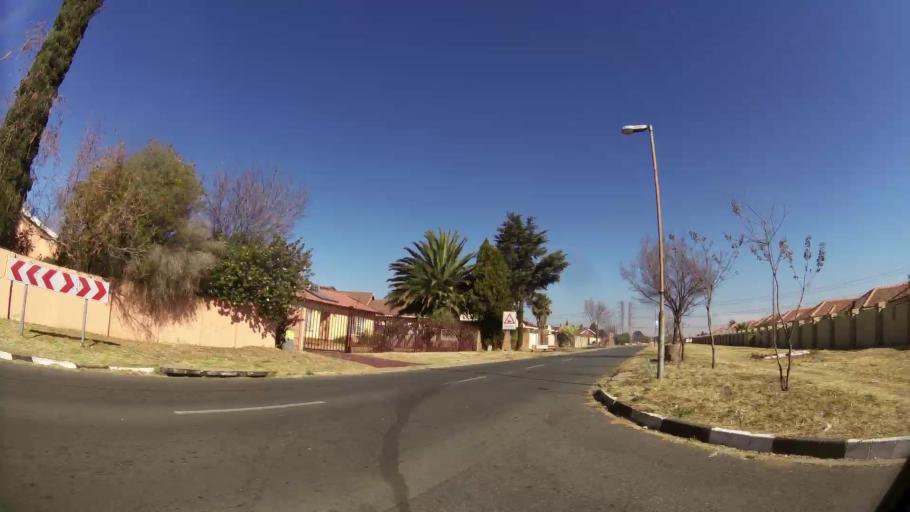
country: ZA
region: Gauteng
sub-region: Ekurhuleni Metropolitan Municipality
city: Germiston
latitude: -26.2427
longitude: 28.1077
